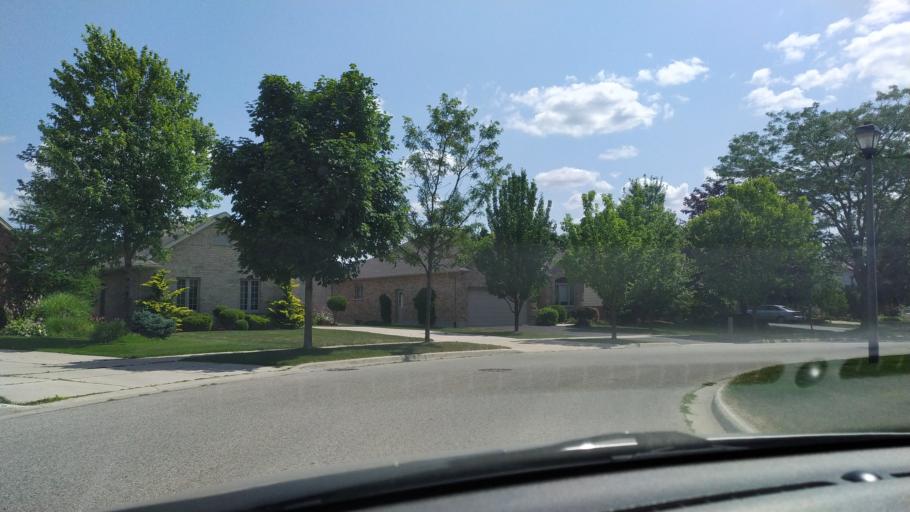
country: CA
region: Ontario
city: Stratford
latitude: 43.3633
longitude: -81.0024
